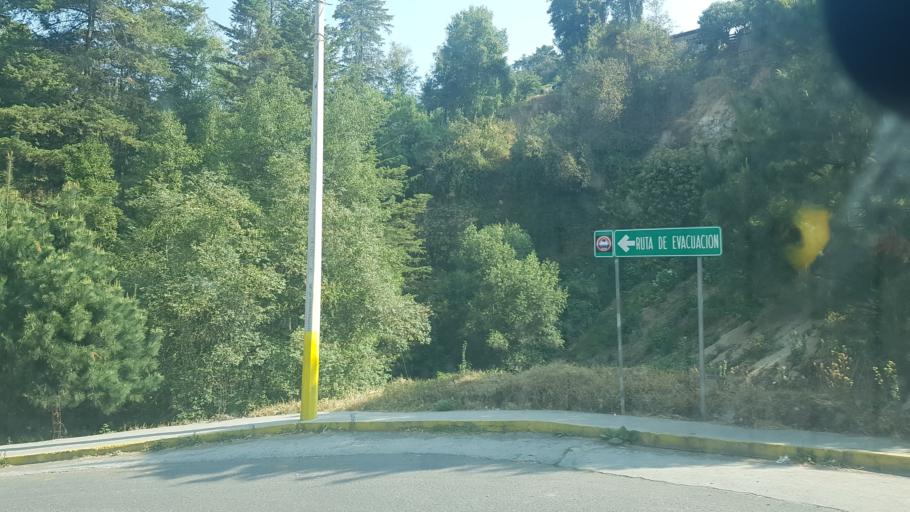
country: MX
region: Morelos
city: Hueyapan
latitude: 18.8887
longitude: -98.6855
